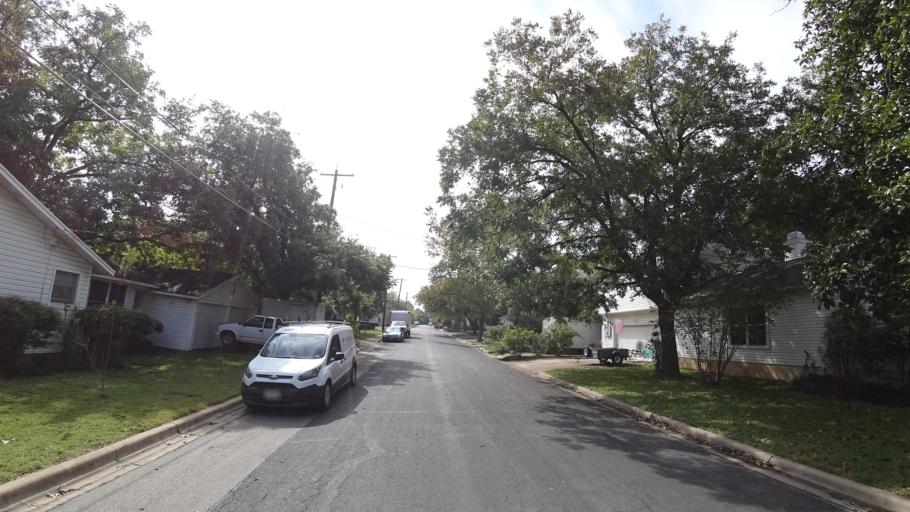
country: US
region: Texas
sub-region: Travis County
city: Rollingwood
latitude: 30.2485
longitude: -97.7783
